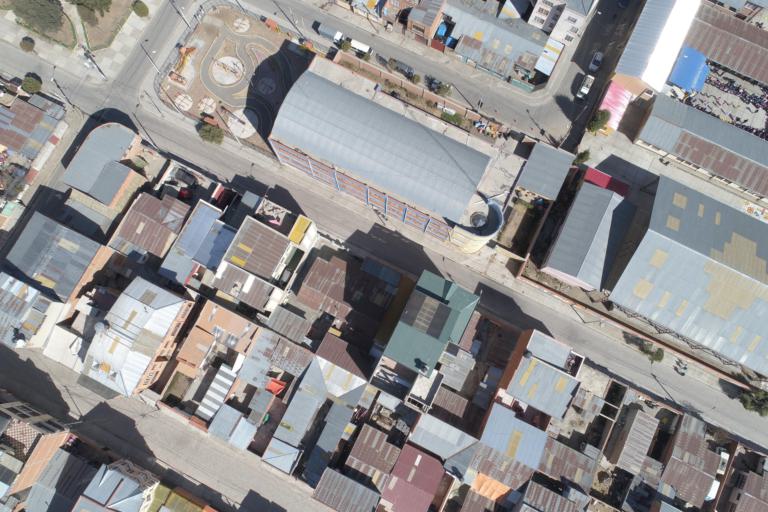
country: BO
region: La Paz
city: La Paz
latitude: -16.5275
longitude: -68.1540
